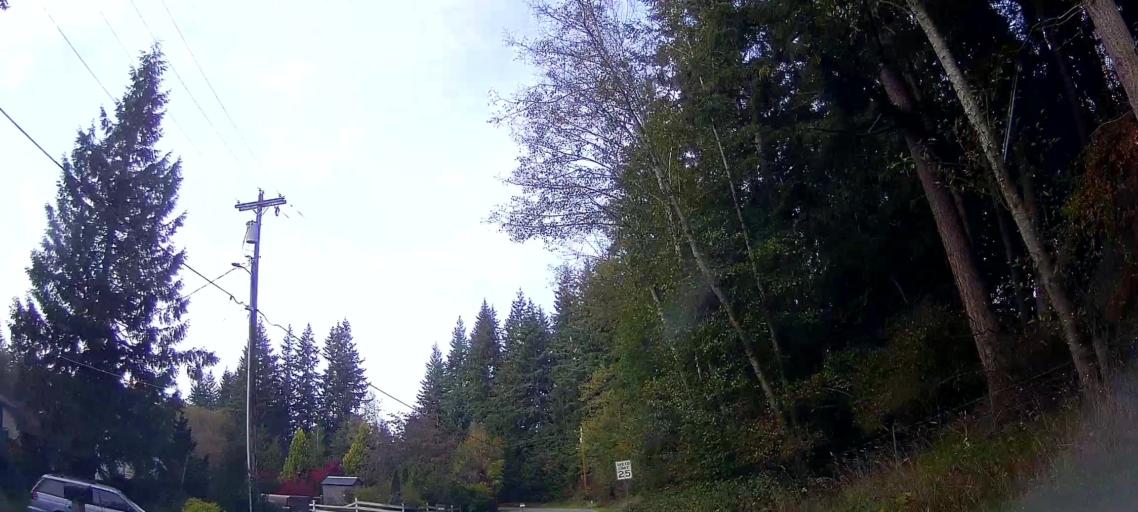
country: US
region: Washington
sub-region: Snohomish County
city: Stanwood
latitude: 48.2865
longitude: -122.3417
